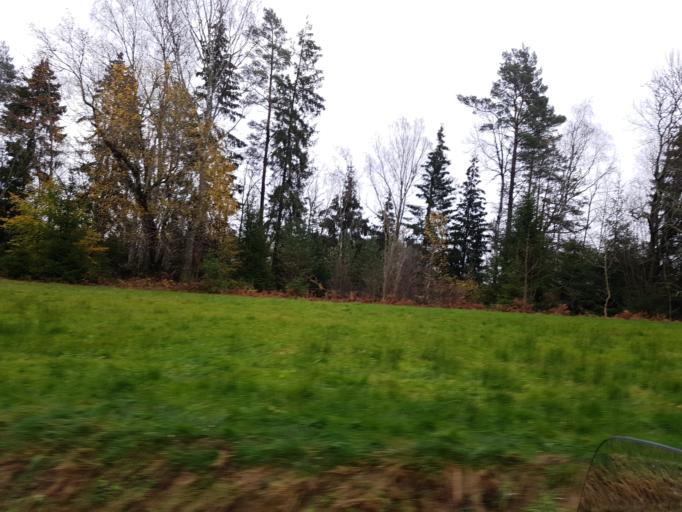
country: SE
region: Vaestra Goetaland
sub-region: Orust
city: Henan
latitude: 58.2349
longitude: 11.7326
